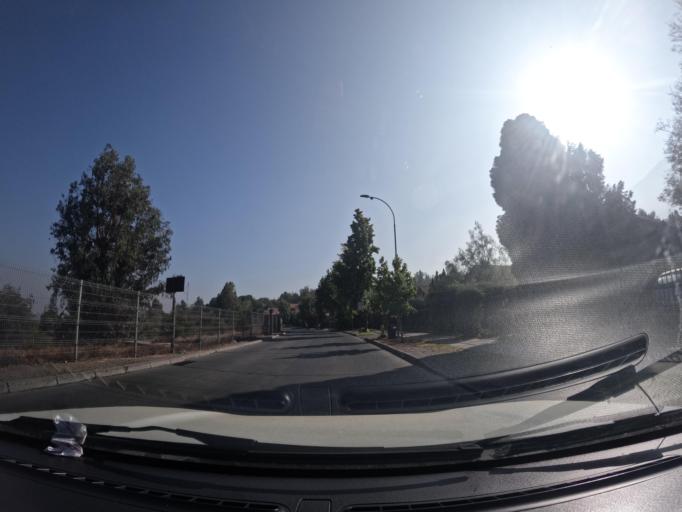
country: CL
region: Santiago Metropolitan
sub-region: Provincia de Santiago
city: Villa Presidente Frei, Nunoa, Santiago, Chile
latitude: -33.4616
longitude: -70.5204
